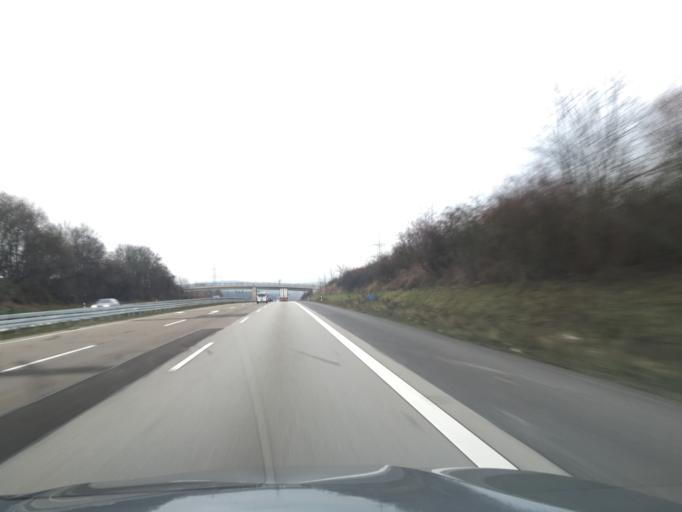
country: DE
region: Hesse
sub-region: Regierungsbezirk Darmstadt
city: Idstein
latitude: 50.2397
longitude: 8.2458
